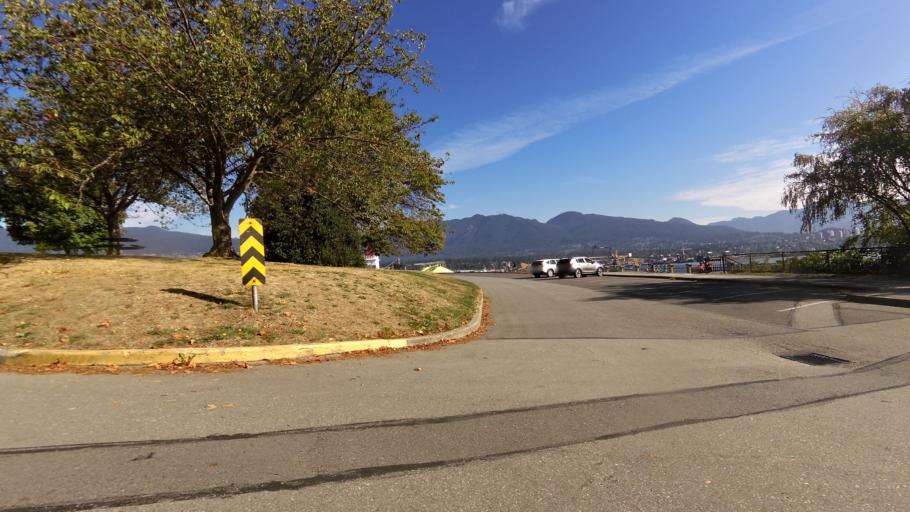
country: CA
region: British Columbia
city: West End
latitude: 49.2999
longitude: -123.1170
